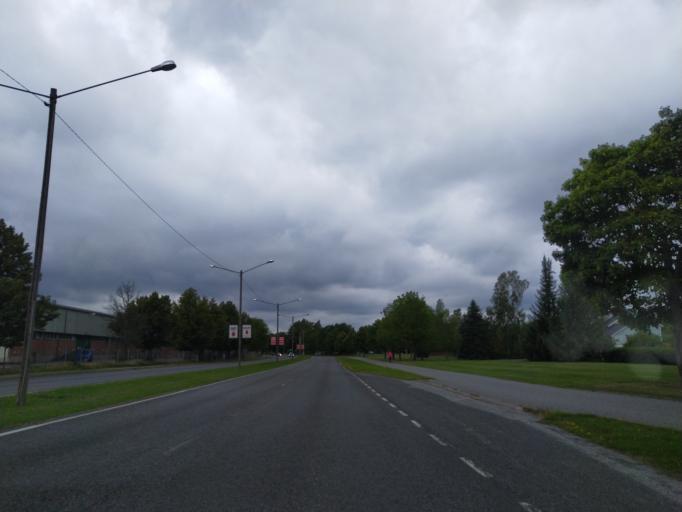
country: FI
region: Varsinais-Suomi
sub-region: Turku
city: Turku
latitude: 60.4478
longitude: 22.3217
